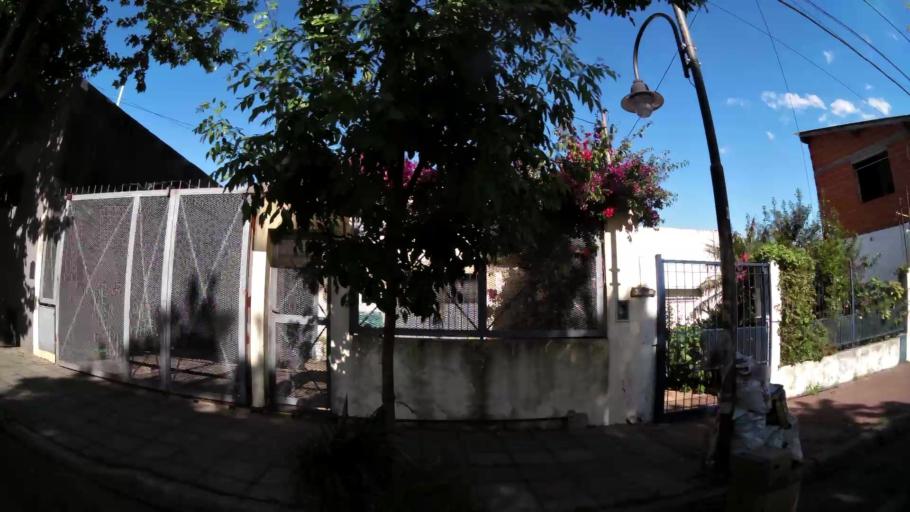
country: AR
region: Buenos Aires
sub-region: Partido de San Isidro
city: San Isidro
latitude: -34.4574
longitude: -58.5390
